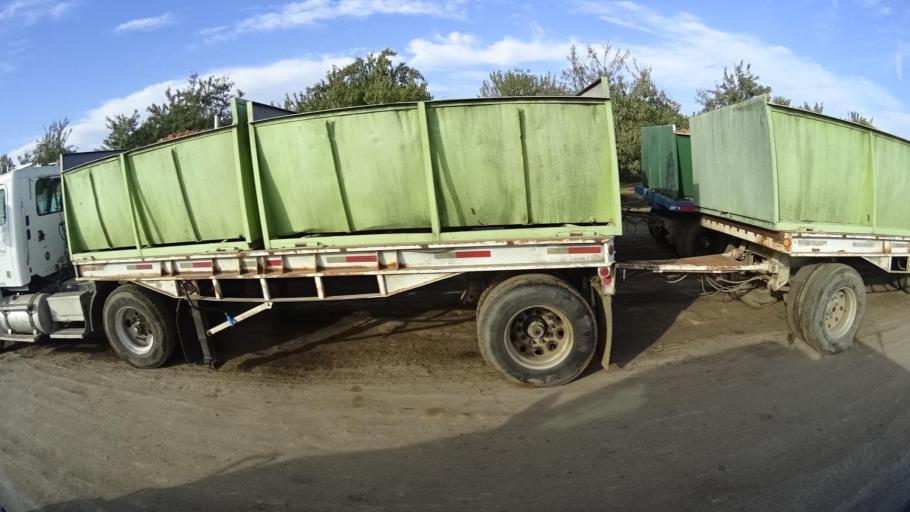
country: US
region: California
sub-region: Kern County
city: Delano
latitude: 35.7837
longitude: -119.2053
